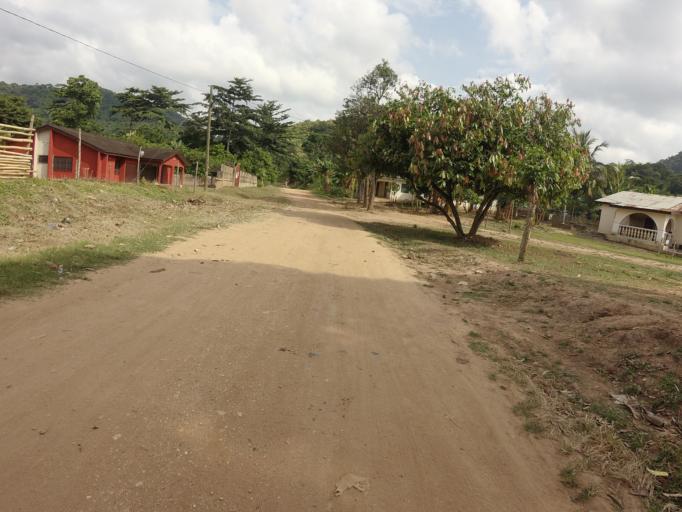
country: GH
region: Volta
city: Kpandu
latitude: 6.8924
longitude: 0.4336
